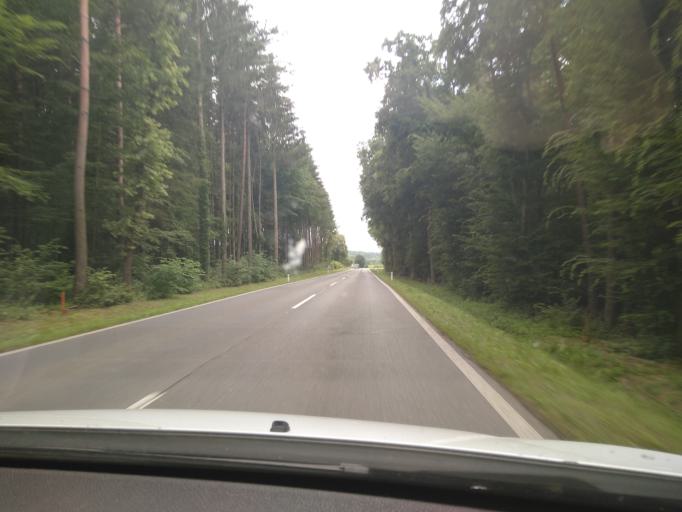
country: AT
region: Burgenland
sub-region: Politischer Bezirk Oberwart
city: Oberschutzen
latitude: 47.3499
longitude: 16.1754
